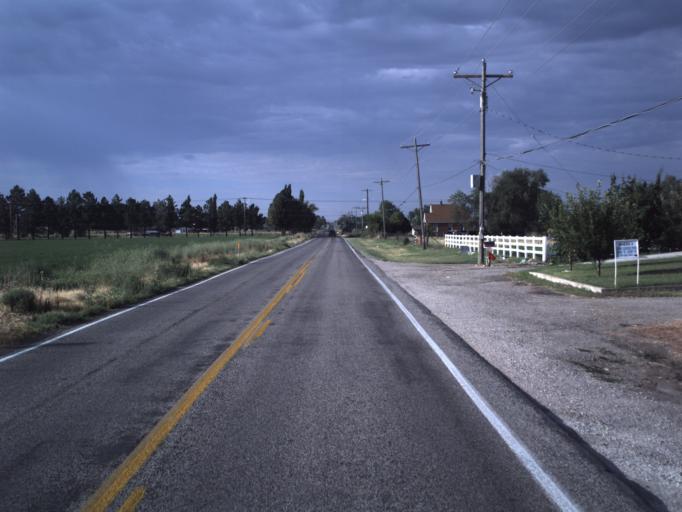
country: US
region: Utah
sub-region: Weber County
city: West Haven
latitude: 41.2223
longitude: -112.0929
